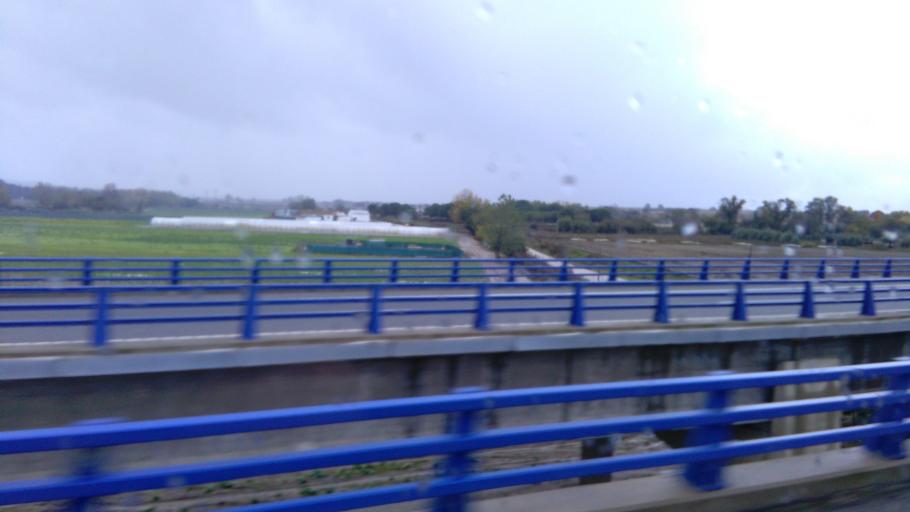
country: ES
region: Madrid
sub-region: Provincia de Madrid
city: Arroyomolinos
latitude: 40.2605
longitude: -3.9515
